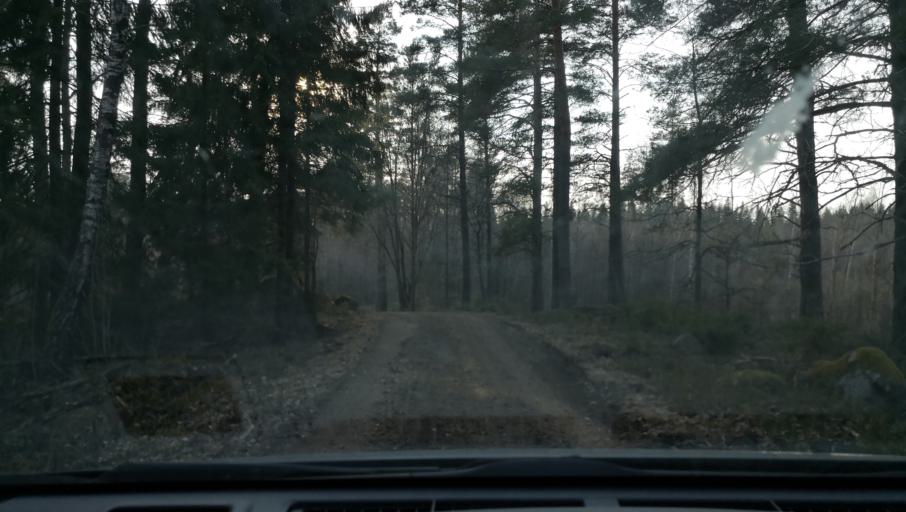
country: SE
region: OErebro
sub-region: Orebro Kommun
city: Hovsta
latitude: 59.3934
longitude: 15.2710
